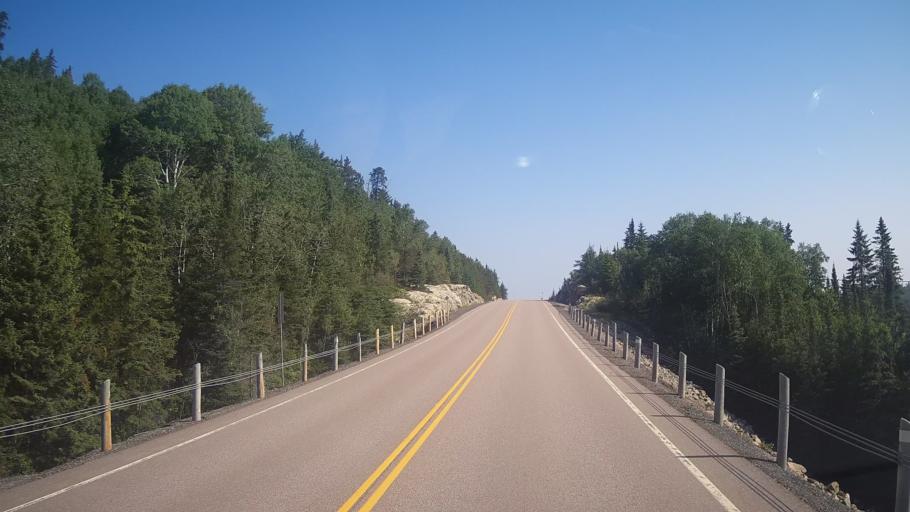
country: CA
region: Ontario
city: Rayside-Balfour
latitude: 46.9899
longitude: -81.6330
